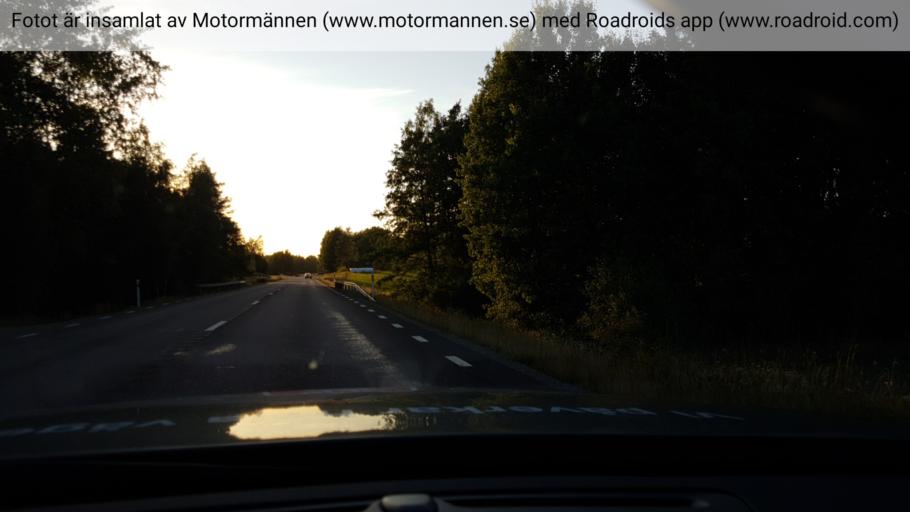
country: SE
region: Vaermland
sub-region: Storfors Kommun
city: Storfors
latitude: 59.4643
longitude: 14.3464
